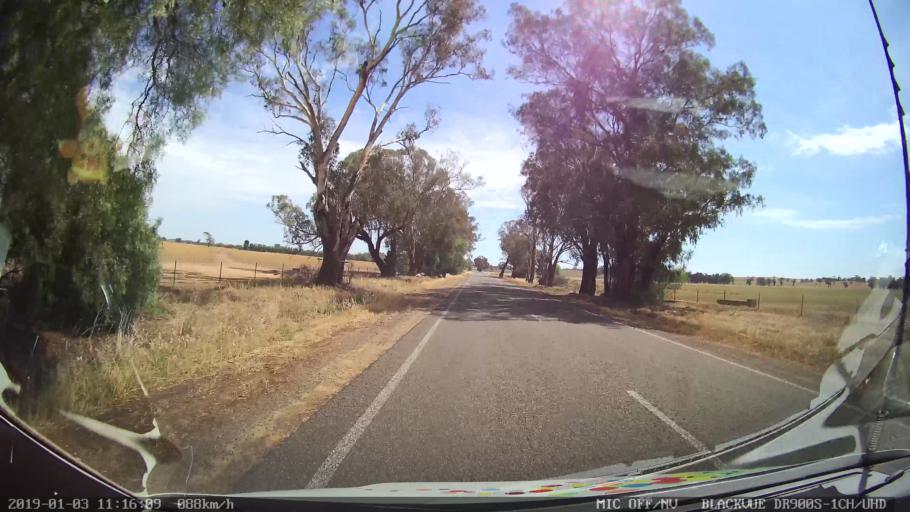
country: AU
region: New South Wales
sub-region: Young
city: Young
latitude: -34.1556
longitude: 148.2691
